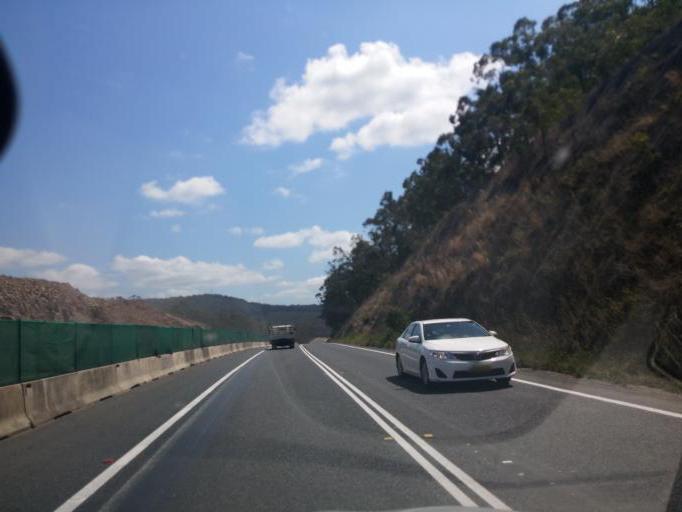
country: AU
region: New South Wales
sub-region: Port Macquarie-Hastings
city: North Shore
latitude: -31.2818
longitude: 152.8141
